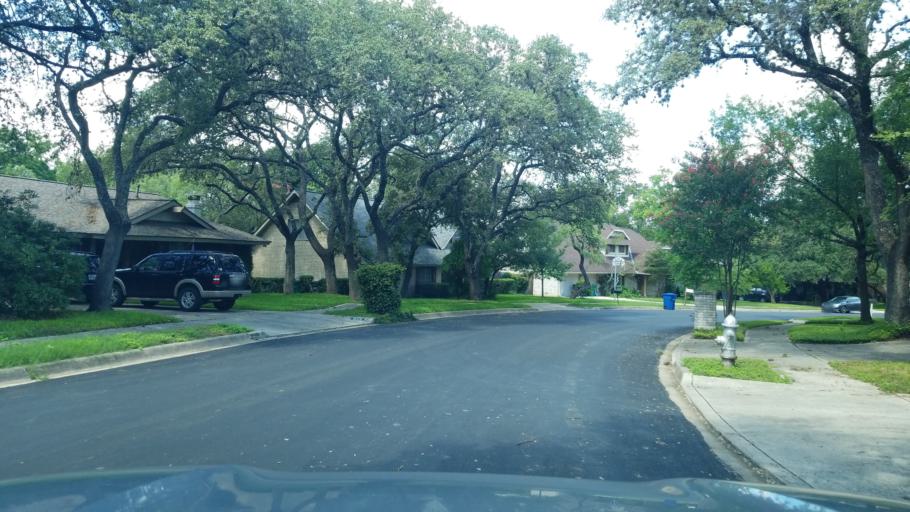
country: US
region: Texas
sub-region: Bexar County
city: Castle Hills
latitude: 29.5454
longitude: -98.5065
